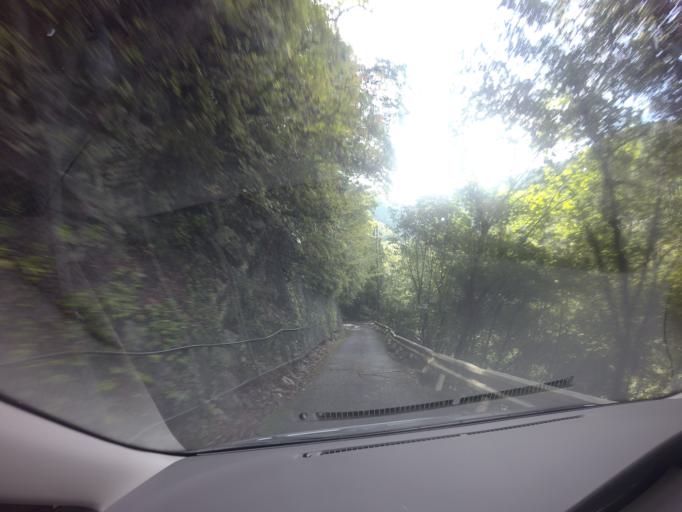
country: JP
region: Wakayama
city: Shingu
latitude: 33.9670
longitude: 135.8436
